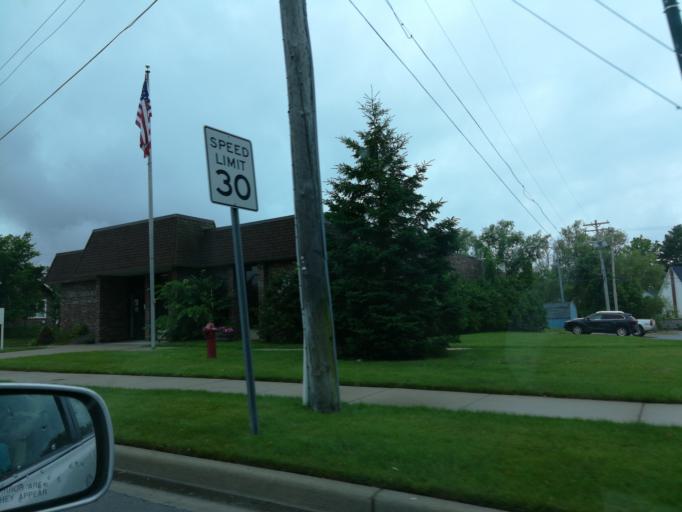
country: US
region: Michigan
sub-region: Iosco County
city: Tawas City
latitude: 44.2654
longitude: -83.5209
